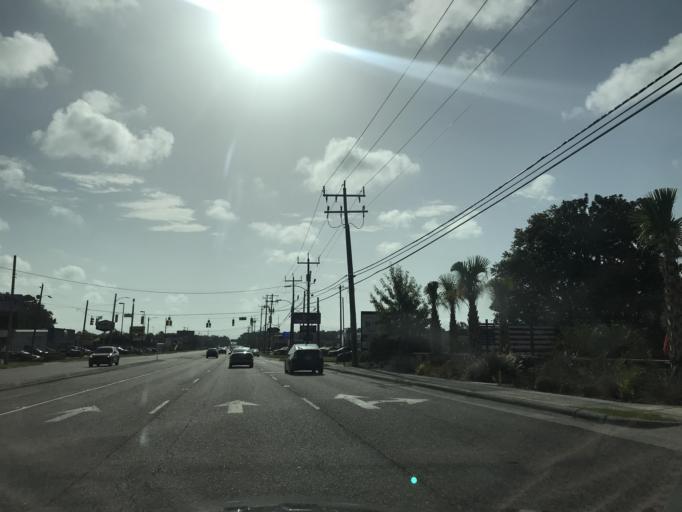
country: US
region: North Carolina
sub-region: New Hanover County
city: Seagate
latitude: 34.2110
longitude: -77.8931
